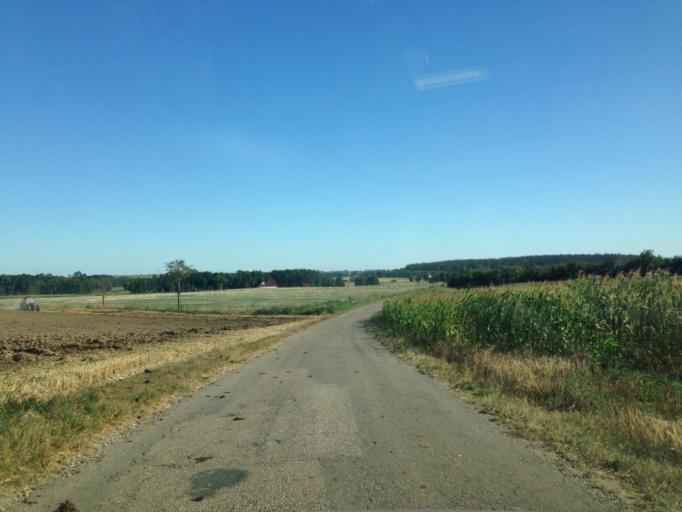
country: PL
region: Kujawsko-Pomorskie
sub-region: Powiat brodnicki
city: Swiedziebnia
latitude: 53.1996
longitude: 19.5288
